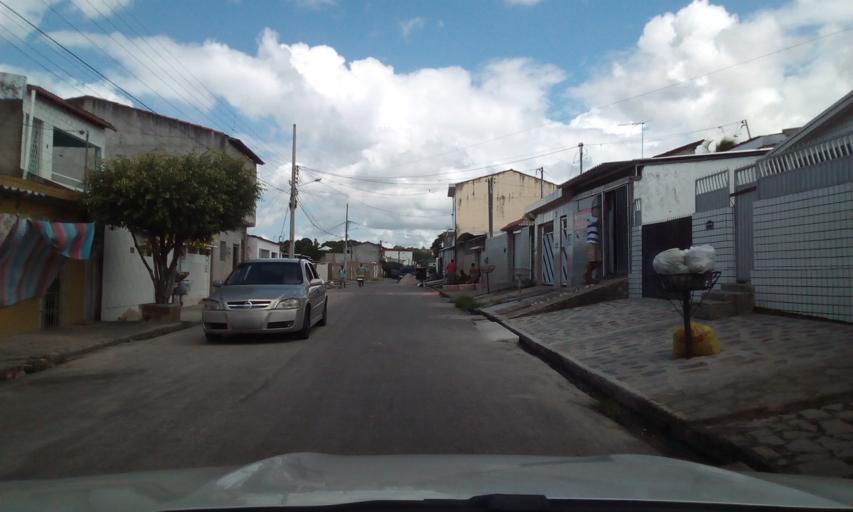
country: BR
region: Paraiba
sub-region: Bayeux
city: Bayeux
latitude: -7.1332
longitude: -34.9203
